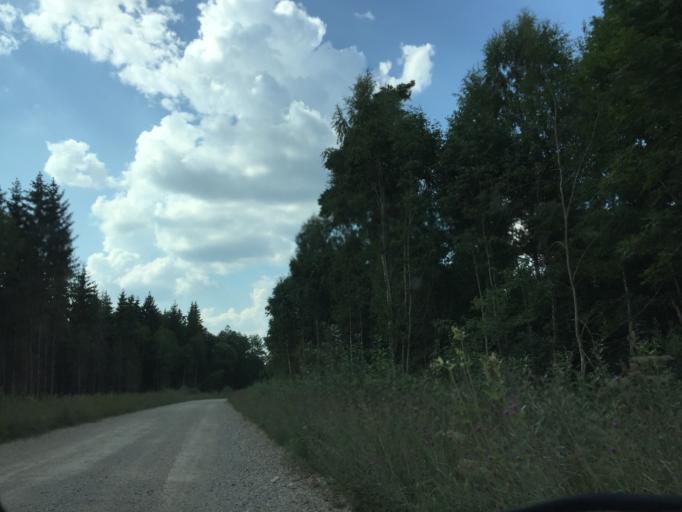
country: LV
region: Auces Novads
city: Auce
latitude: 56.4144
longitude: 22.9881
